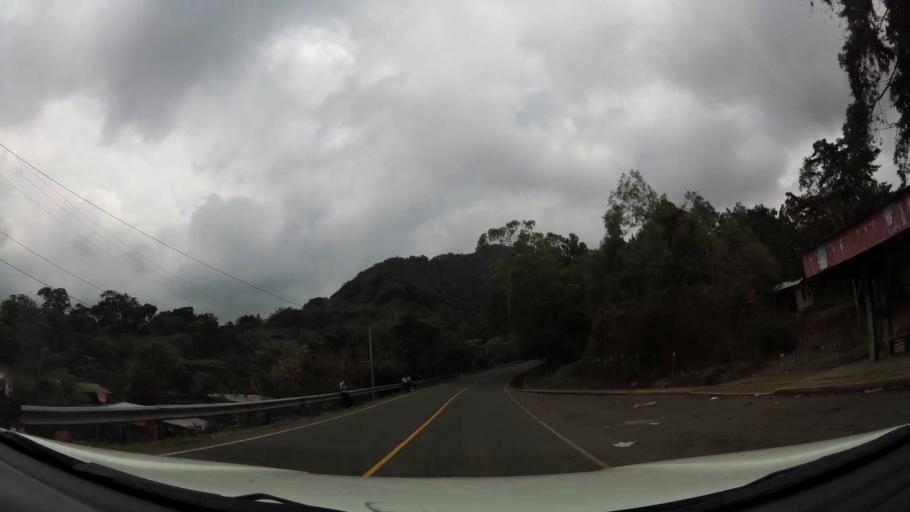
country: NI
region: Matagalpa
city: Matagalpa
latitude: 12.9961
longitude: -85.9219
